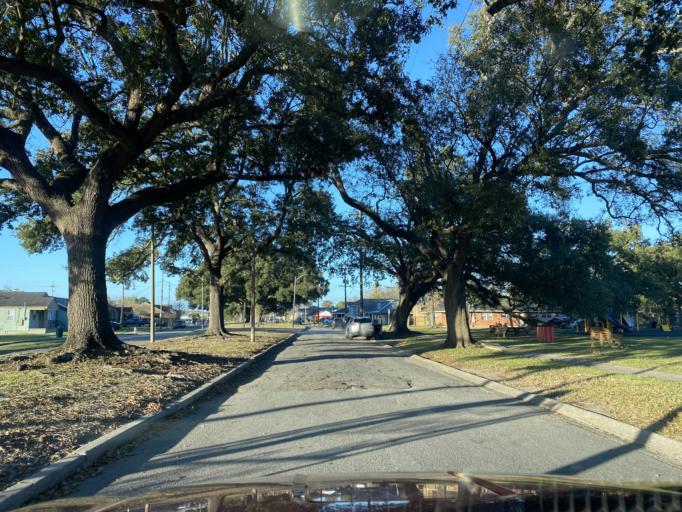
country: US
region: Louisiana
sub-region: Orleans Parish
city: New Orleans
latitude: 30.0133
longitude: -90.0557
